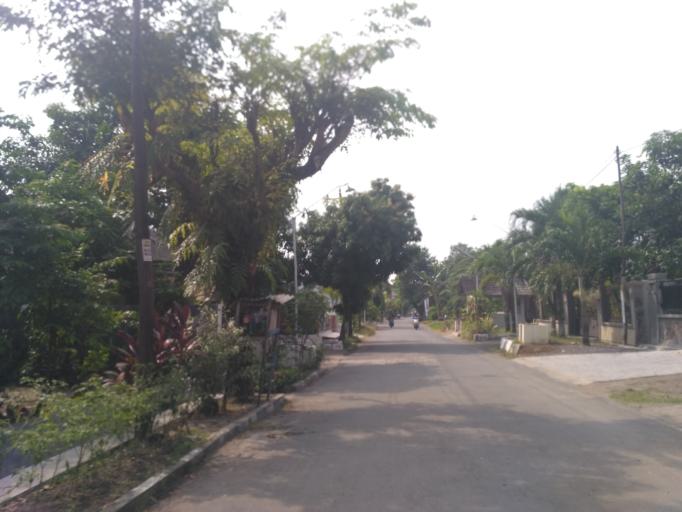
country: ID
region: Central Java
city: Mranggen
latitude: -7.0478
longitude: 110.4809
